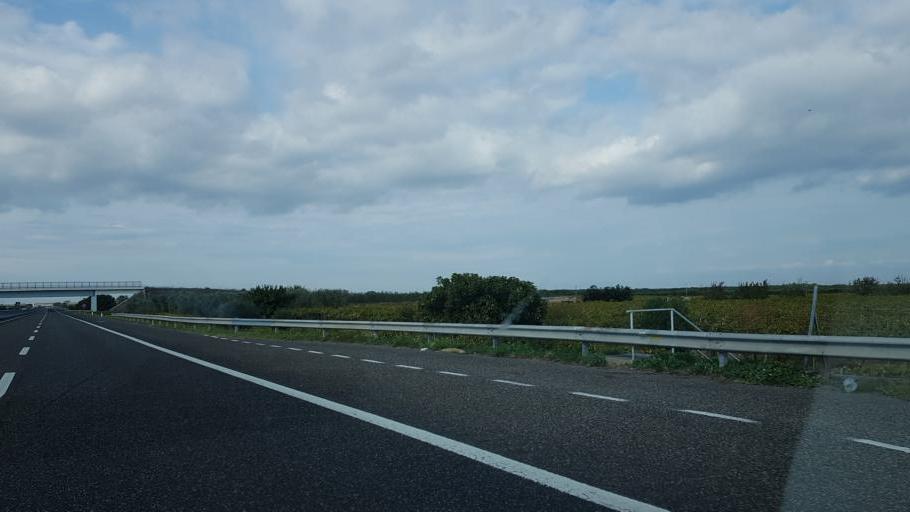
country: IT
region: Apulia
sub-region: Provincia di Foggia
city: Cerignola
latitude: 41.3313
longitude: 15.8691
